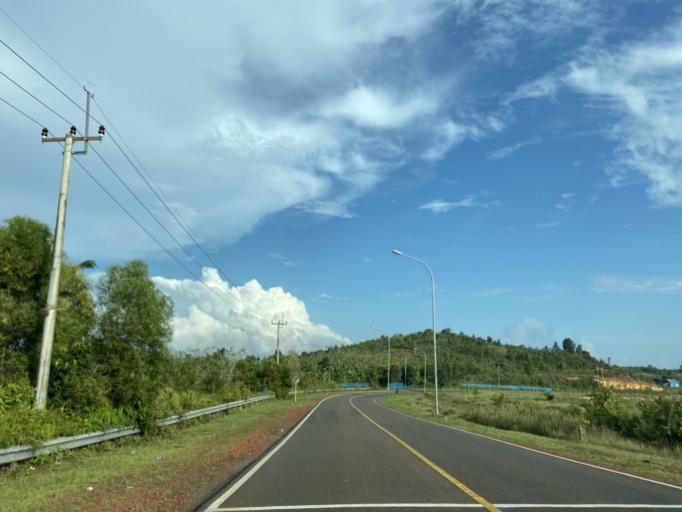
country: SG
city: Singapore
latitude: 0.9506
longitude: 104.0540
